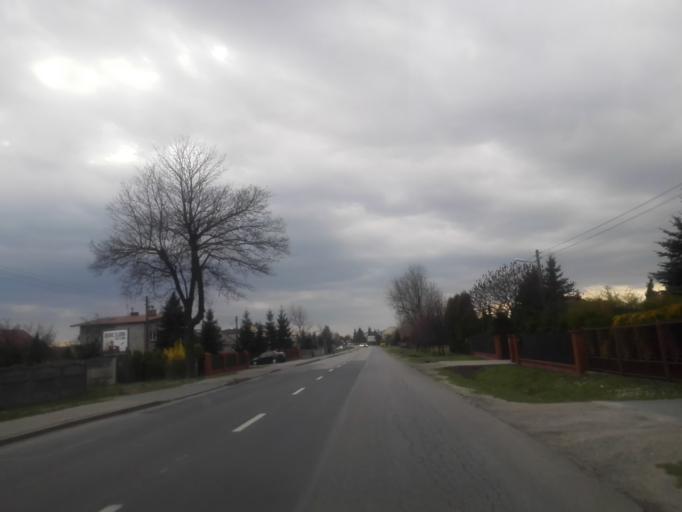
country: PL
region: Silesian Voivodeship
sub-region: Powiat czestochowski
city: Redziny
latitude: 50.8386
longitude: 19.2245
